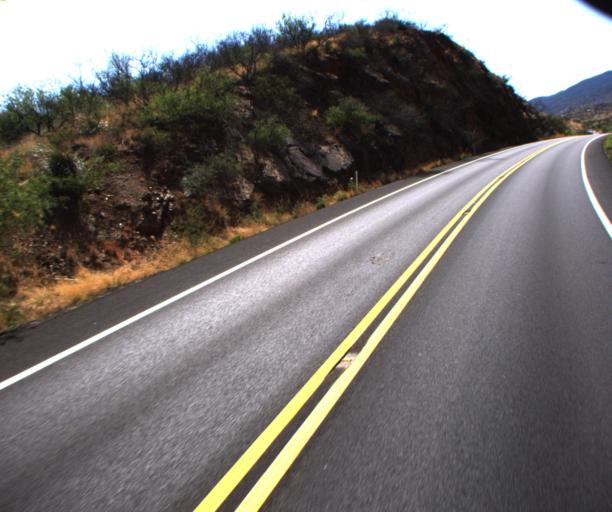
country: US
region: Arizona
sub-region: Cochise County
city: Bisbee
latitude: 31.5054
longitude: -110.0082
